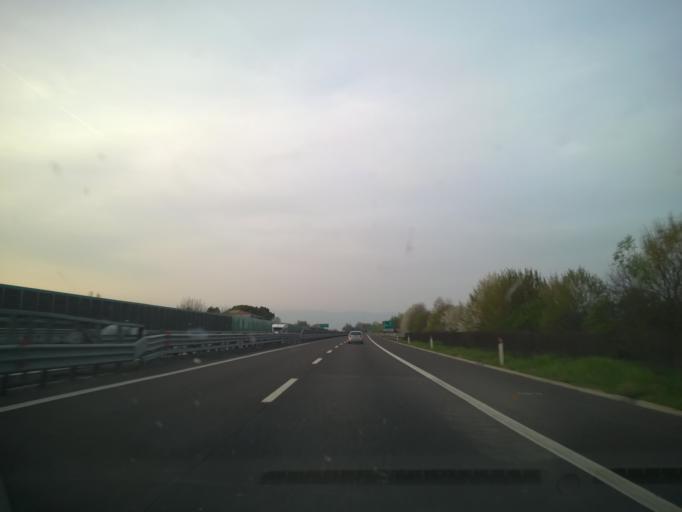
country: IT
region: Veneto
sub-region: Provincia di Vicenza
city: Villaggio Montegrappa
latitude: 45.5572
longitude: 11.6153
